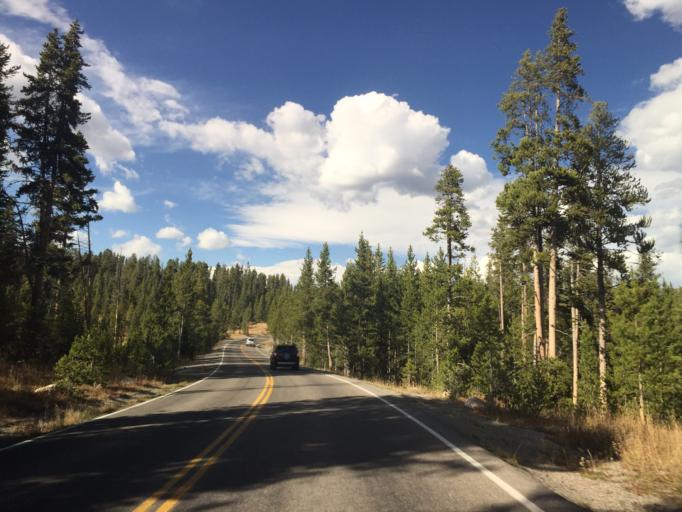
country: US
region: Montana
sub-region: Gallatin County
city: West Yellowstone
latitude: 44.7136
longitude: -110.5042
